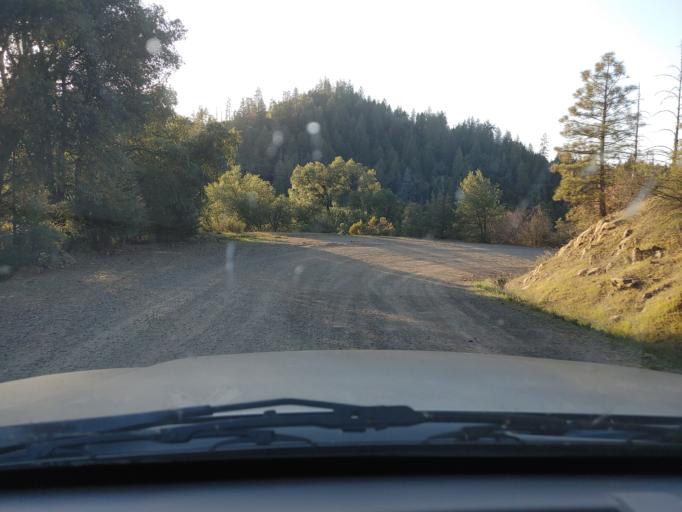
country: US
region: California
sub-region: Shasta County
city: Bella Vista
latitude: 40.8372
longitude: -122.0177
